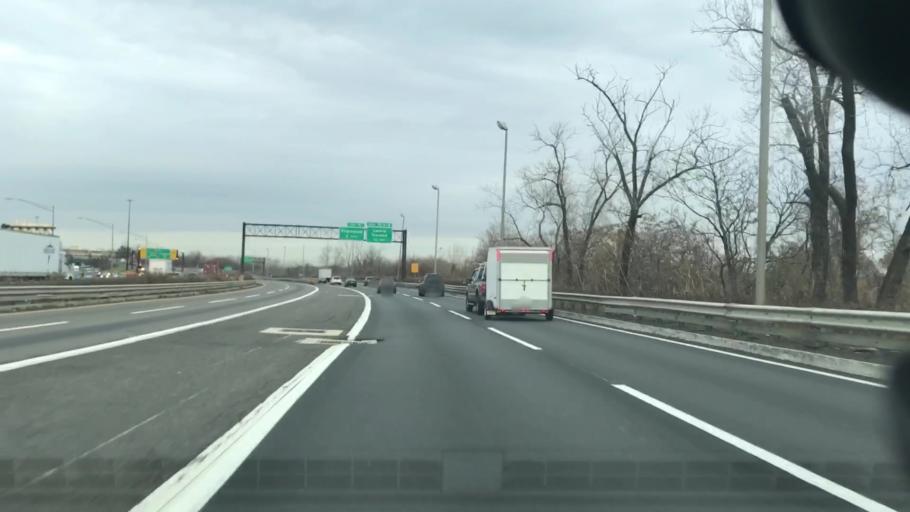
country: US
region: New Jersey
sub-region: Bergen County
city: Ridgefield Park
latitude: 40.8581
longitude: -74.0119
